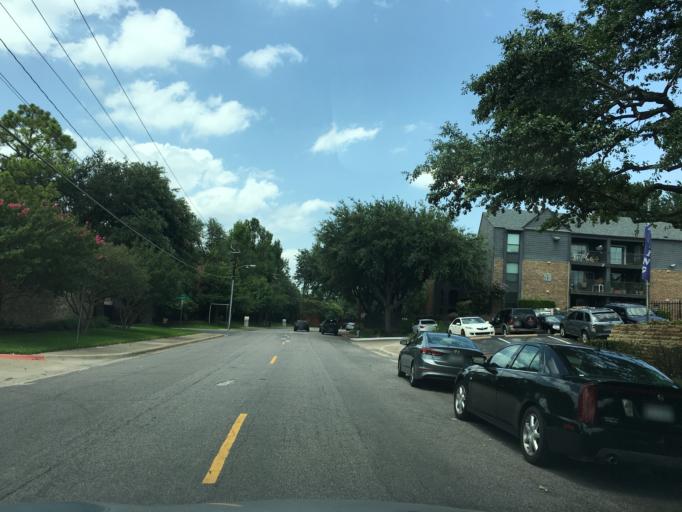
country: US
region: Texas
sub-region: Dallas County
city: University Park
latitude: 32.8933
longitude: -96.7750
